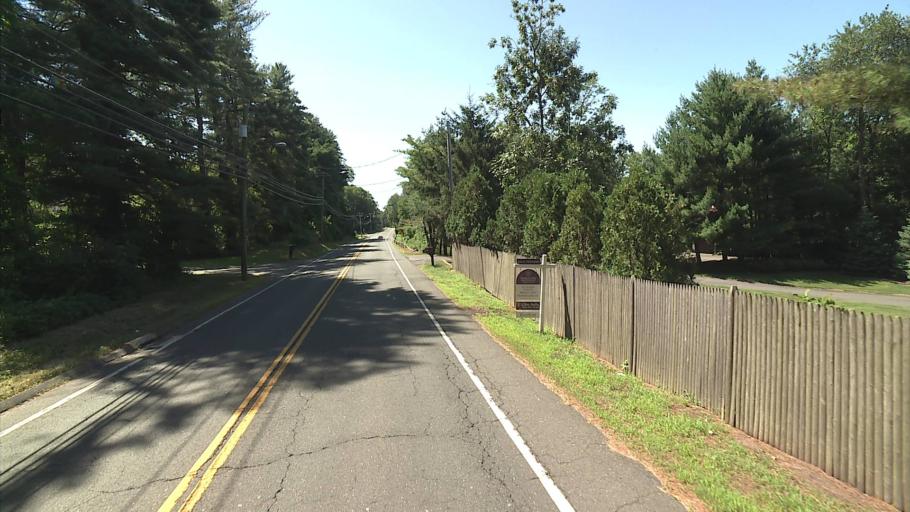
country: US
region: Connecticut
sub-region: Hartford County
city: Farmington
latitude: 41.7649
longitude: -72.8199
